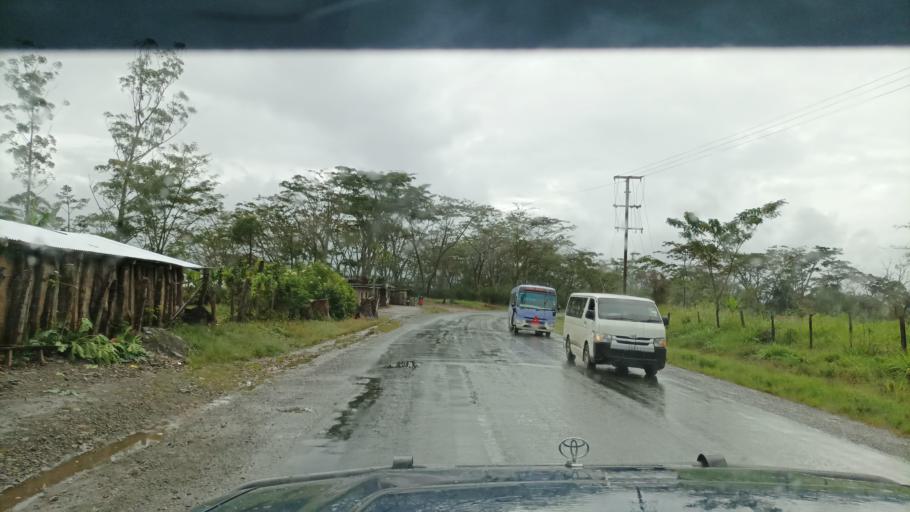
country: PG
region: Jiwaka
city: Minj
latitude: -5.8437
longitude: 144.6020
